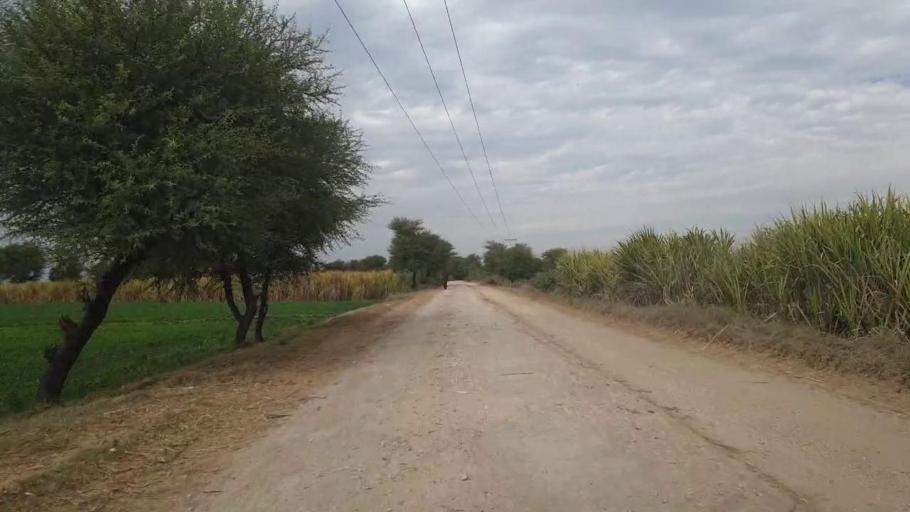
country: PK
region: Sindh
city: Jhol
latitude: 26.0201
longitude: 68.8749
